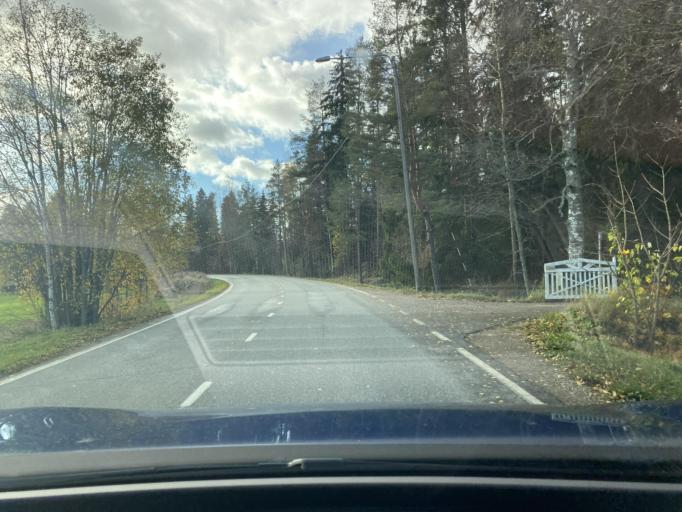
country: FI
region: Varsinais-Suomi
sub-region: Loimaa
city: Aura
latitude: 60.7117
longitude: 22.5953
